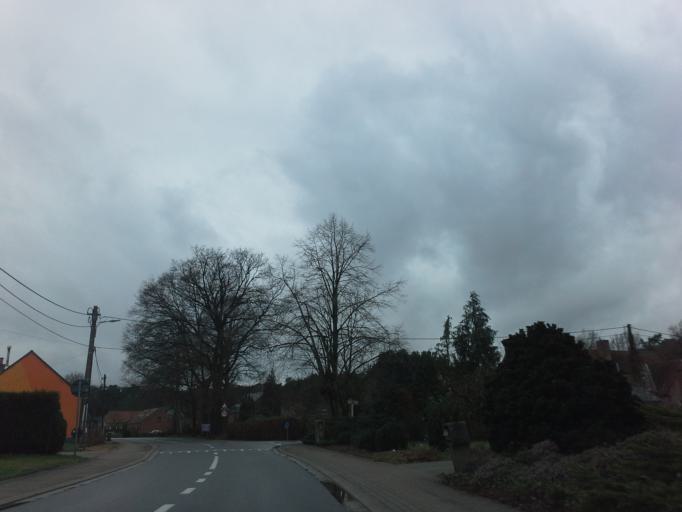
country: BE
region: Flanders
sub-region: Provincie Antwerpen
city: Meerhout
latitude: 51.1437
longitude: 5.1045
